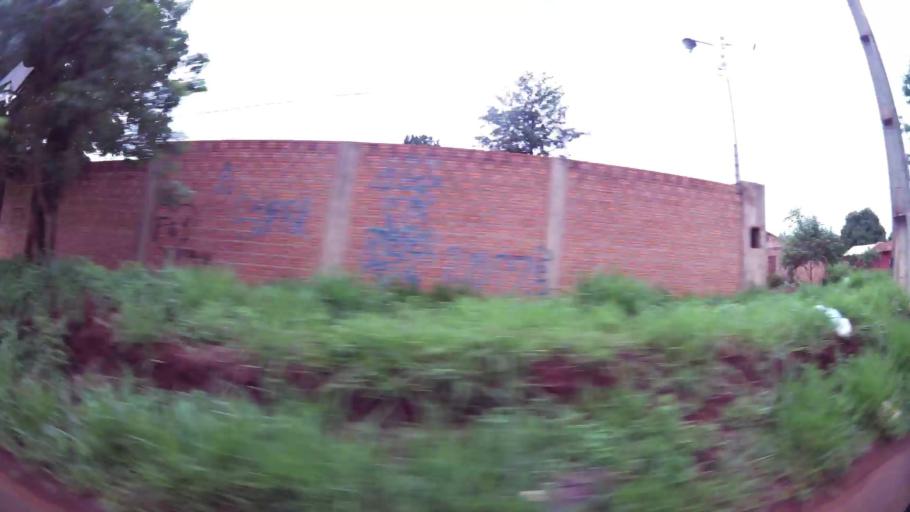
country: PY
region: Alto Parana
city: Presidente Franco
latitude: -25.5131
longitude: -54.6908
